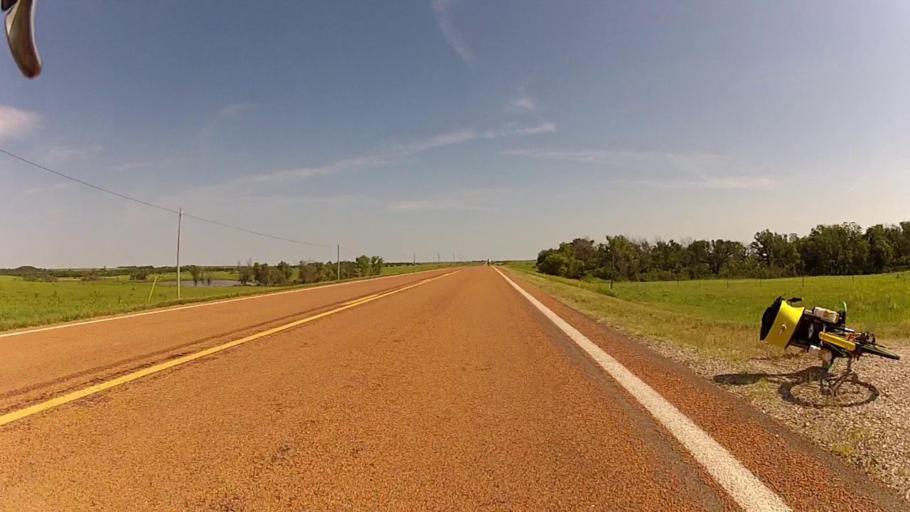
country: US
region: Kansas
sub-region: Cowley County
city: Winfield
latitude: 37.0835
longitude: -96.6436
